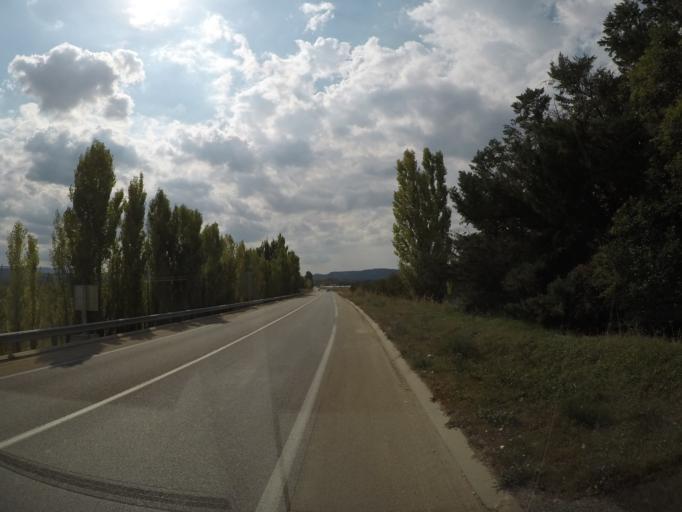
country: FR
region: Provence-Alpes-Cote d'Azur
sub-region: Departement du Vaucluse
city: Pertuis
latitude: 43.6590
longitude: 5.4944
